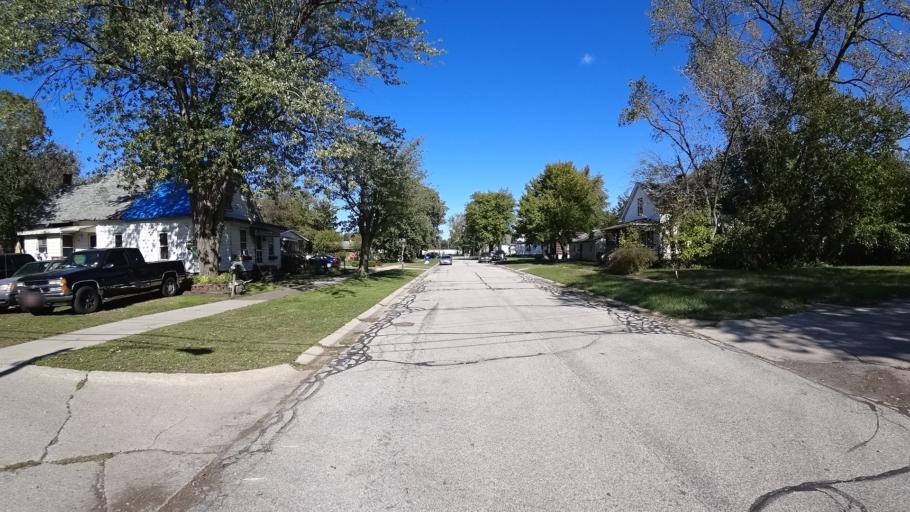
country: US
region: Indiana
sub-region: LaPorte County
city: Michigan City
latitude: 41.7073
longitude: -86.9207
